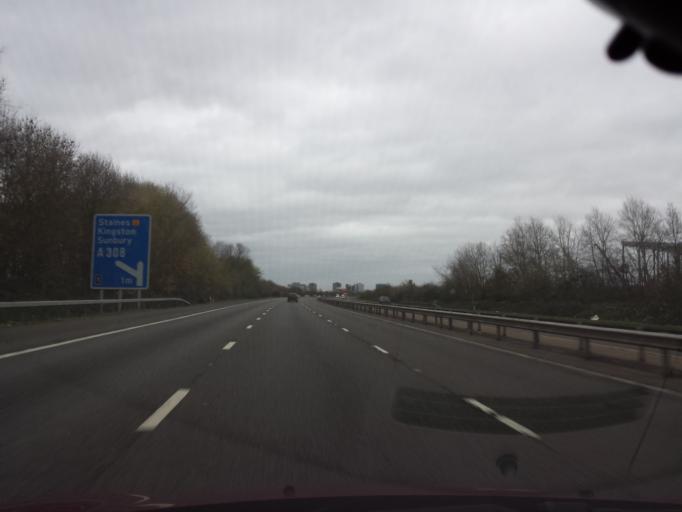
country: GB
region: England
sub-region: Surrey
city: Shepperton
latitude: 51.4065
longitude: -0.4441
